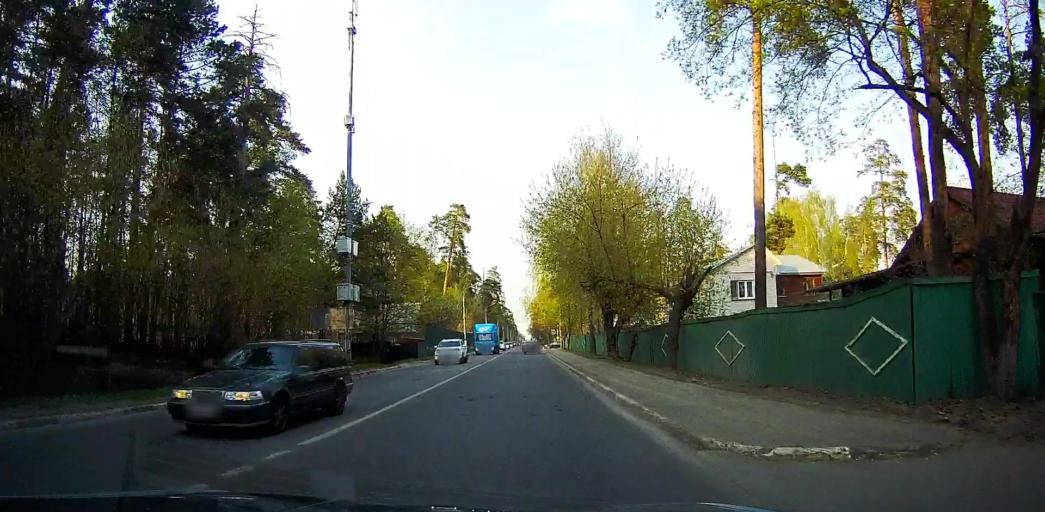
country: RU
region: Moskovskaya
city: Kratovo
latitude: 55.5733
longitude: 38.1853
